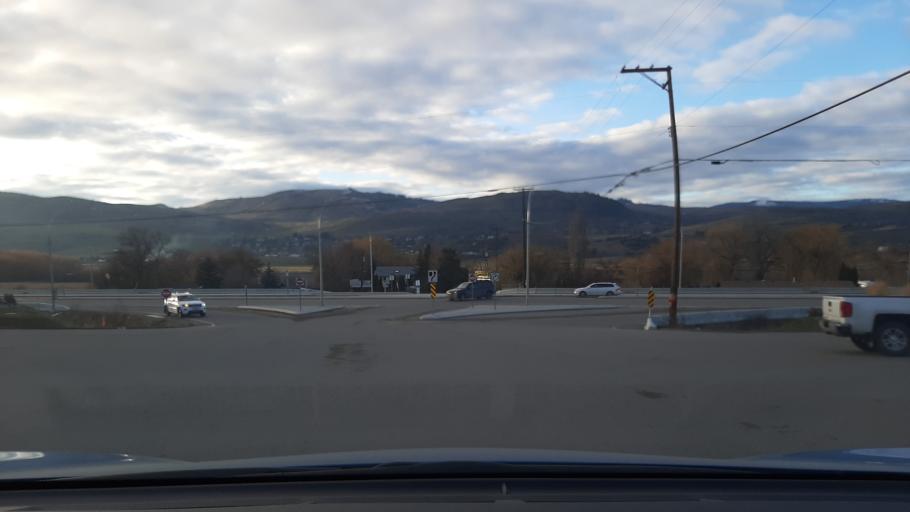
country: CA
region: British Columbia
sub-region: Regional District of North Okanagan
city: Vernon
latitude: 50.2975
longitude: -119.2539
